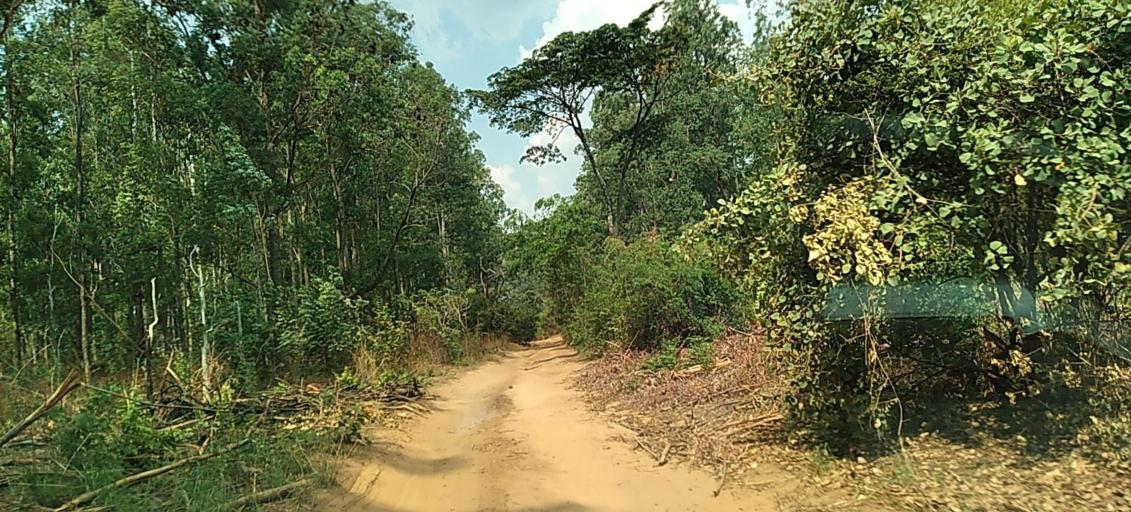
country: ZM
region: Copperbelt
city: Chingola
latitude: -12.7386
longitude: 27.7657
